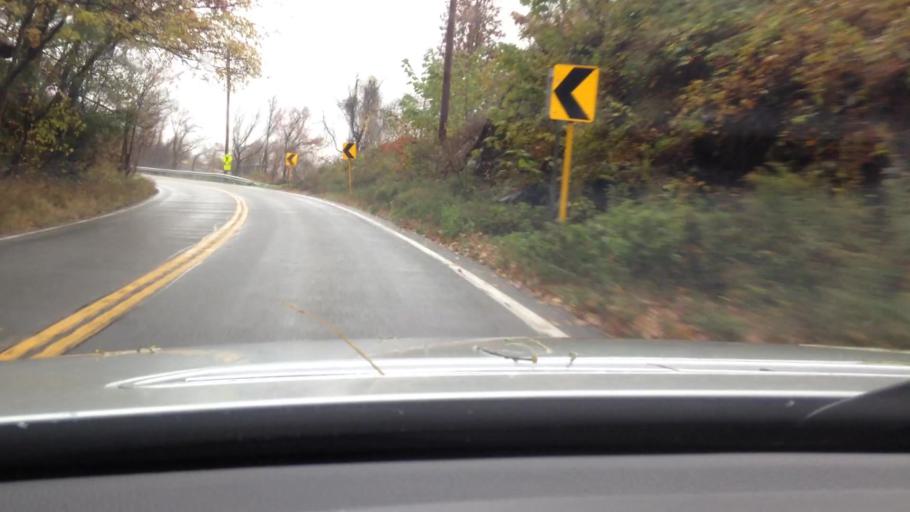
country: US
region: New York
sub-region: Orange County
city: Cornwall-on-Hudson
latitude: 41.4513
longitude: -73.9827
